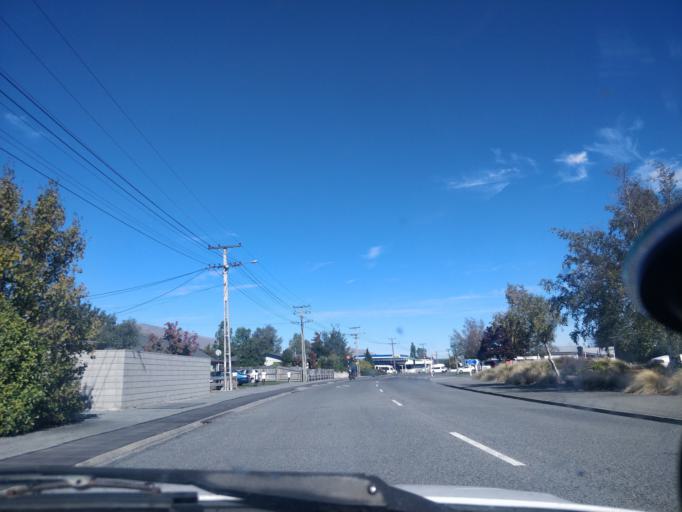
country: NZ
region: Canterbury
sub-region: Timaru District
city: Pleasant Point
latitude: -44.2563
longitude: 170.1010
